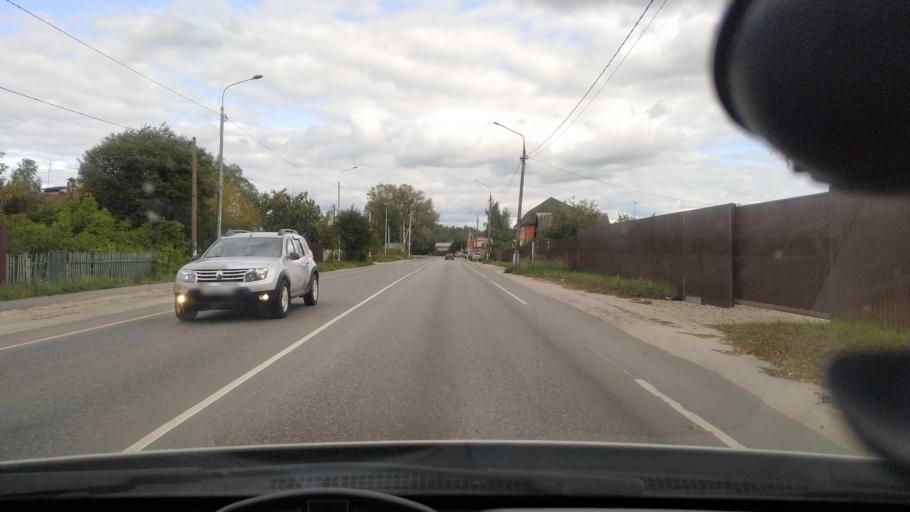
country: RU
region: Moskovskaya
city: Likino-Dulevo
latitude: 55.7266
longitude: 38.9617
